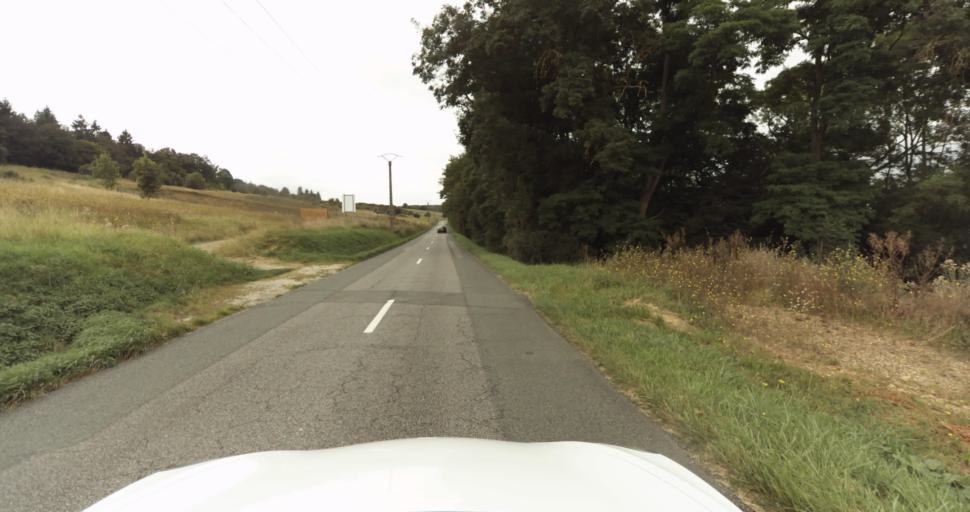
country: FR
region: Haute-Normandie
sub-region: Departement de l'Eure
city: Arnieres-sur-Iton
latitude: 49.0102
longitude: 1.1054
